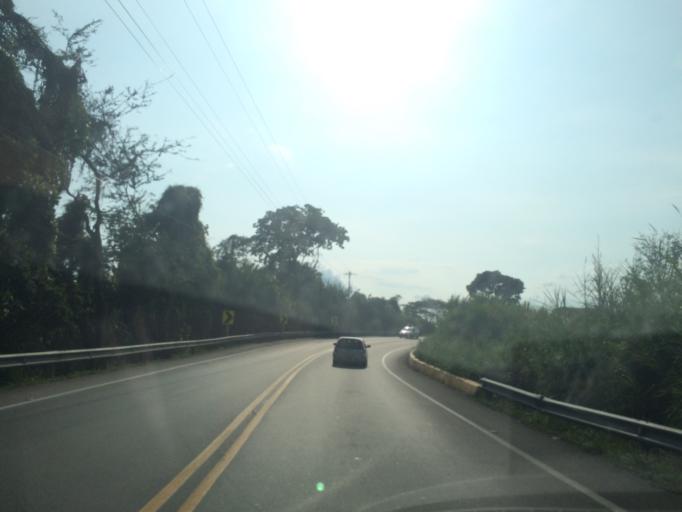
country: CO
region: Quindio
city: La Tebaida
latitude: 4.4460
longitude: -75.8262
